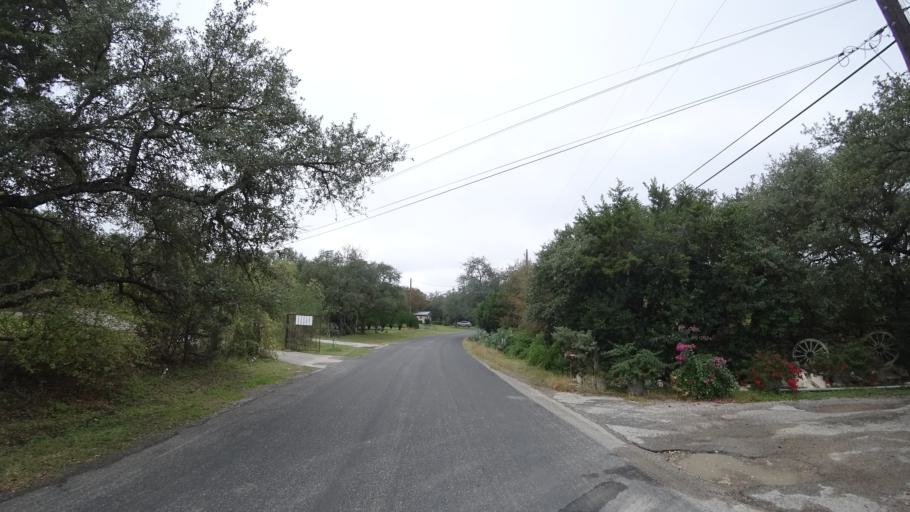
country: US
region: Texas
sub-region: Travis County
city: Barton Creek
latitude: 30.2367
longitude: -97.9038
